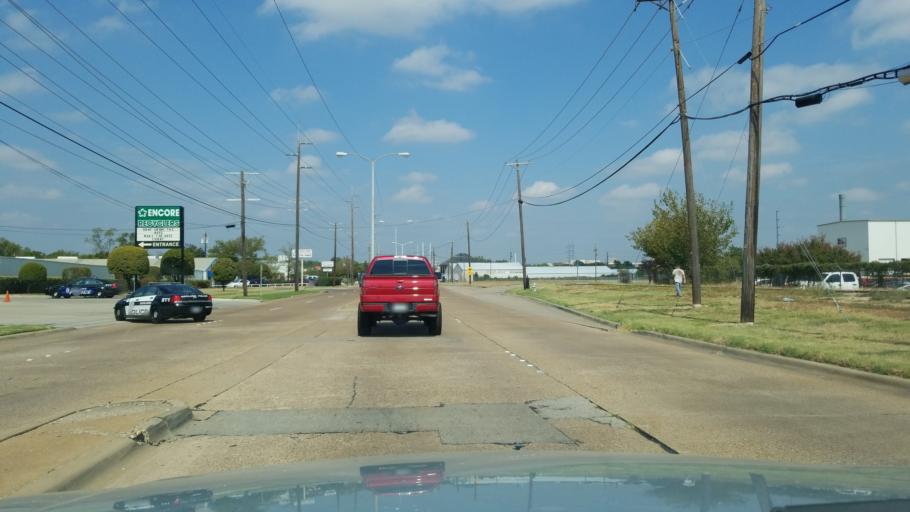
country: US
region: Texas
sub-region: Dallas County
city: Garland
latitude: 32.9103
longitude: -96.6654
